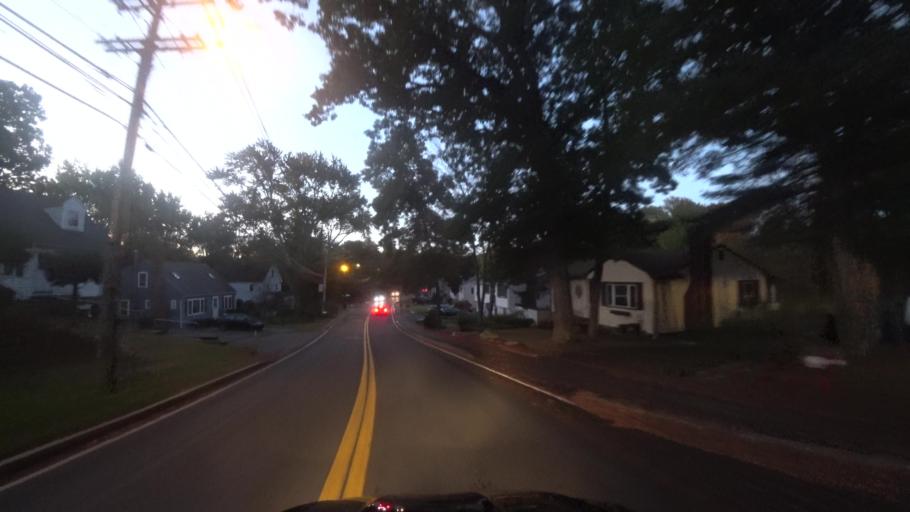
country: US
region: Massachusetts
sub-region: Middlesex County
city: Wakefield
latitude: 42.5048
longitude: -71.0469
